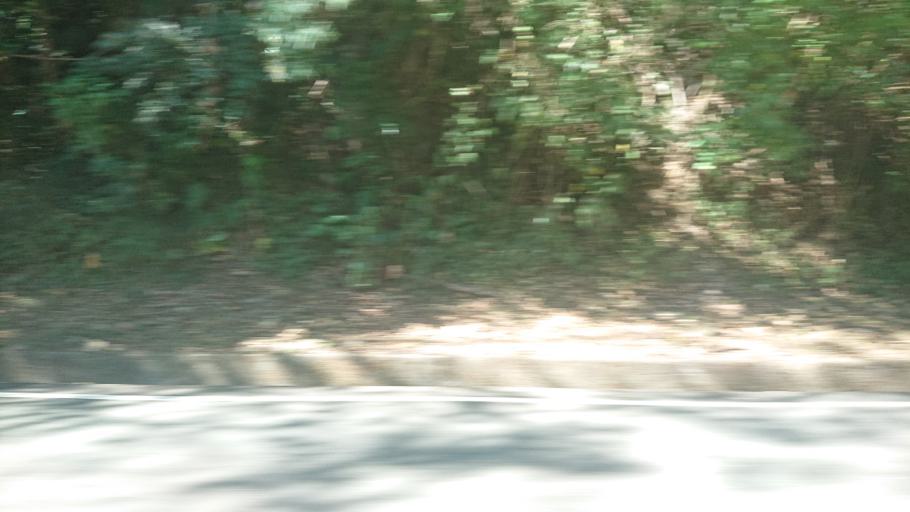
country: TW
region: Taiwan
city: Lugu
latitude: 23.4804
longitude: 120.7359
